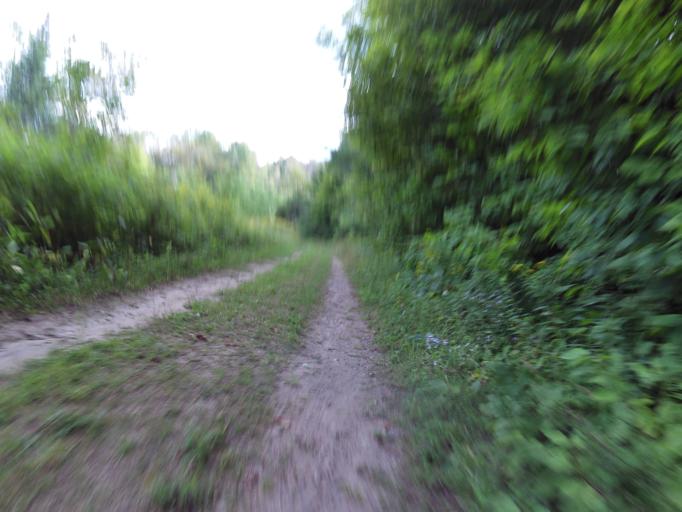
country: CA
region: Quebec
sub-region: Outaouais
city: Wakefield
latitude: 45.6425
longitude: -75.9980
